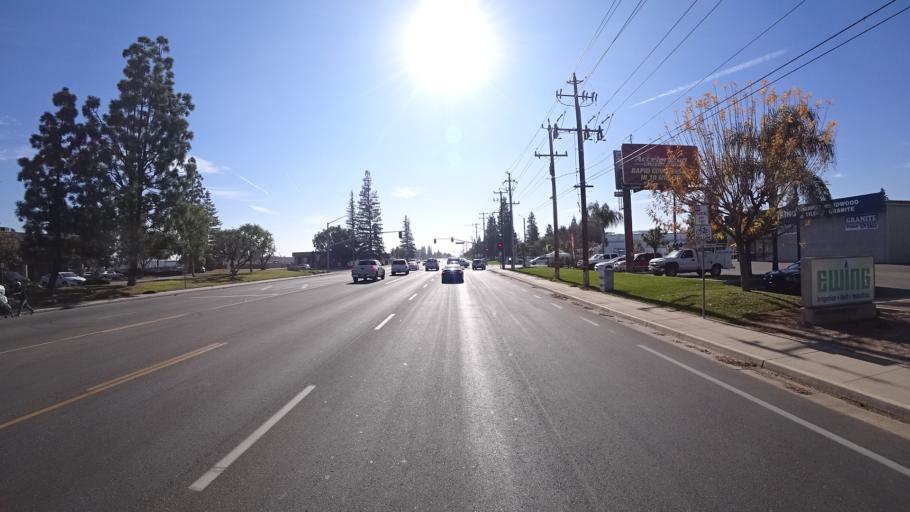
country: US
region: California
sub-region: Kern County
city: Greenacres
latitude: 35.3138
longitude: -119.0745
